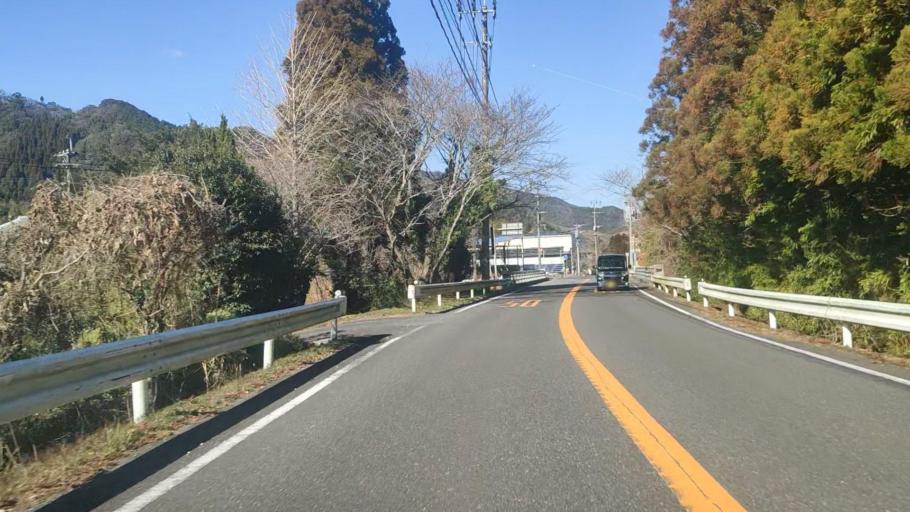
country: JP
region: Oita
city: Saiki
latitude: 32.9013
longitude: 131.9341
